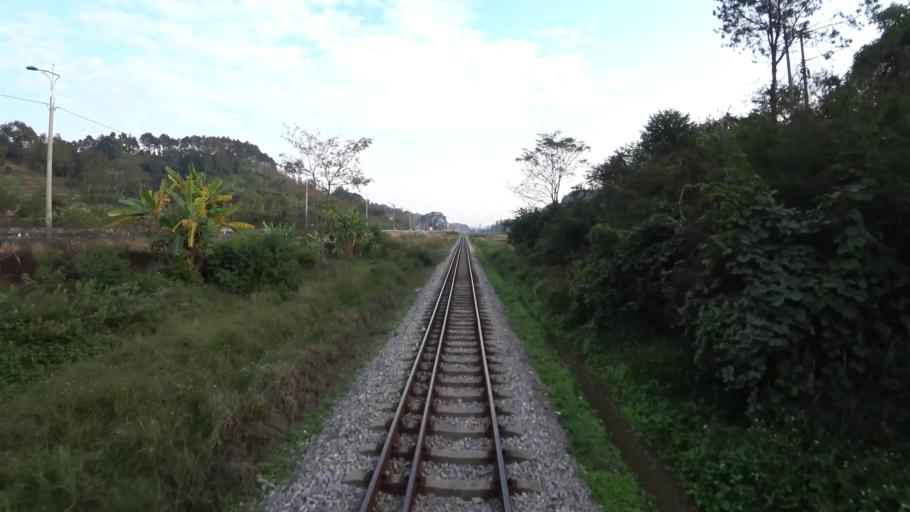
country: VN
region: Lang Son
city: Thi Tran Cao Loc
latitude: 21.9046
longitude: 106.7359
